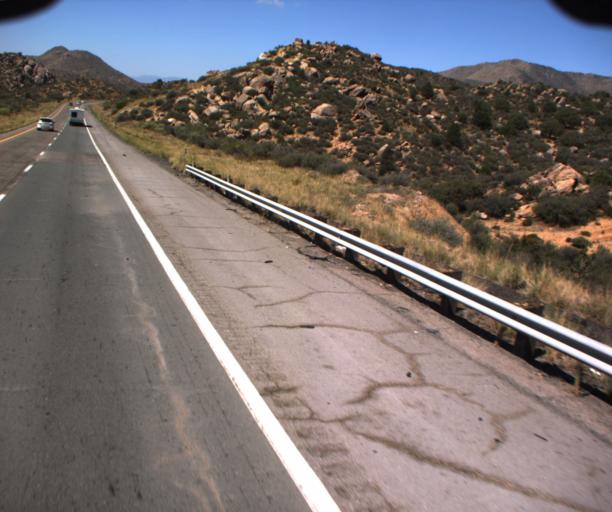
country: US
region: Arizona
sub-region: Mohave County
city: Peach Springs
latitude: 35.1770
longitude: -113.4982
